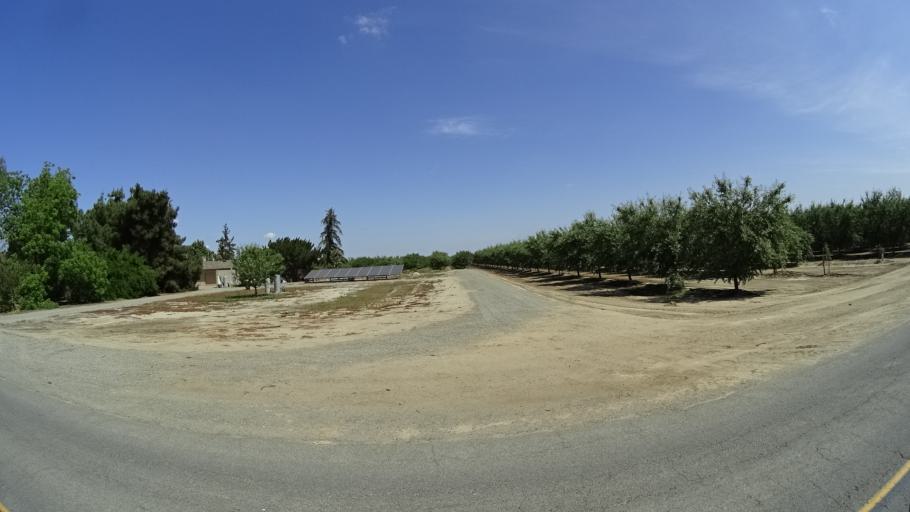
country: US
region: California
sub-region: Kings County
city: Home Garden
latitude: 36.2695
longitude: -119.5644
